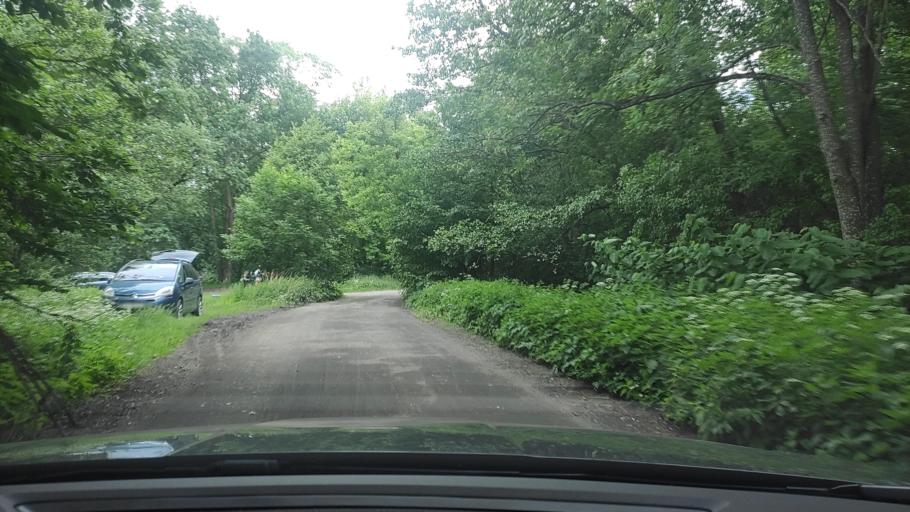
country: PL
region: Greater Poland Voivodeship
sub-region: Powiat poznanski
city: Pobiedziska
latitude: 52.5056
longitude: 17.2065
